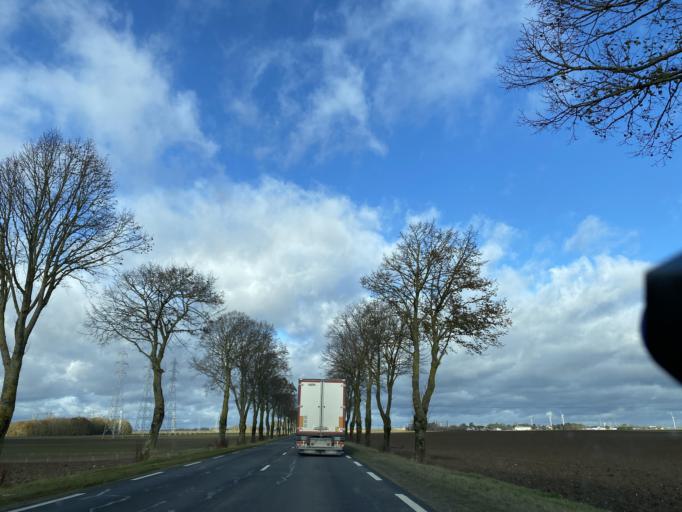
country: FR
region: Centre
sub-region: Departement du Loiret
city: Artenay
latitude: 48.1015
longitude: 1.8646
